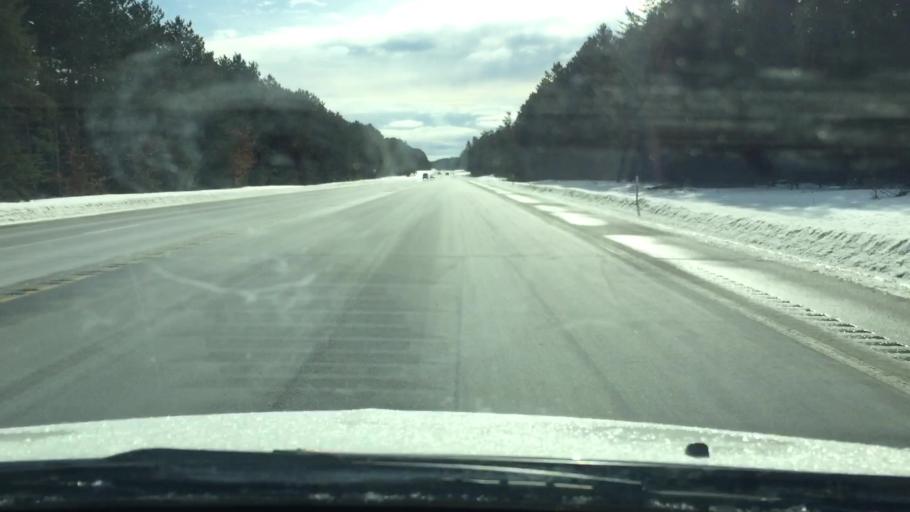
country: US
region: Michigan
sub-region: Kalkaska County
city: Kalkaska
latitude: 44.7910
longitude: -85.1520
